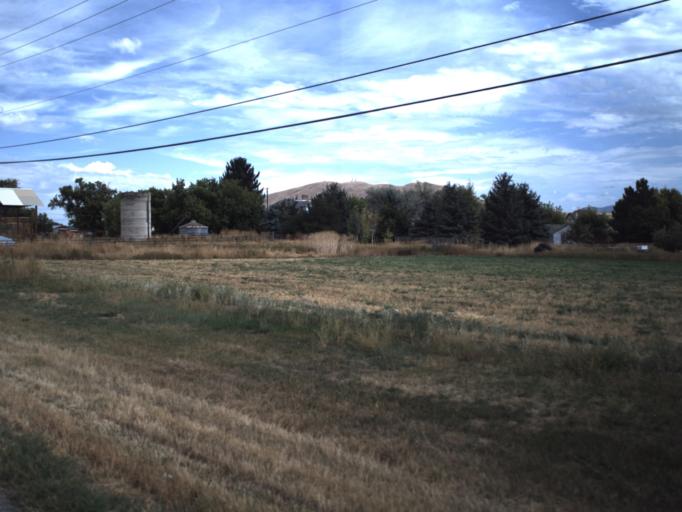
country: US
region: Utah
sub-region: Cache County
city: Benson
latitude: 41.8610
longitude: -111.9998
